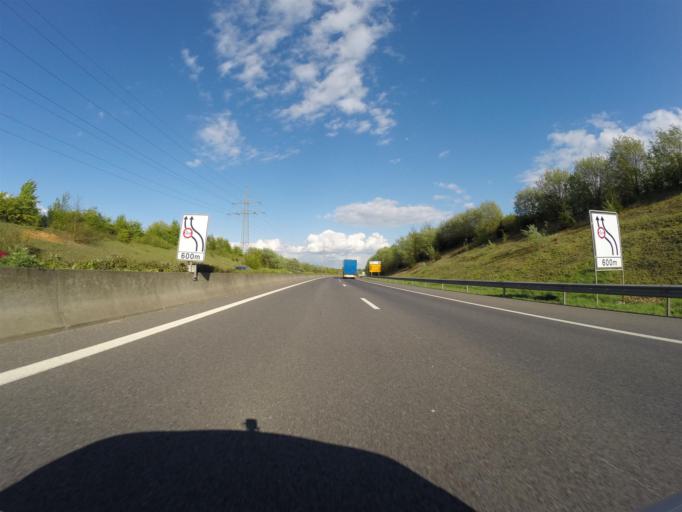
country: LU
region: Luxembourg
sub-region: Canton d'Esch-sur-Alzette
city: Frisange
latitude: 49.5105
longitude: 6.1767
